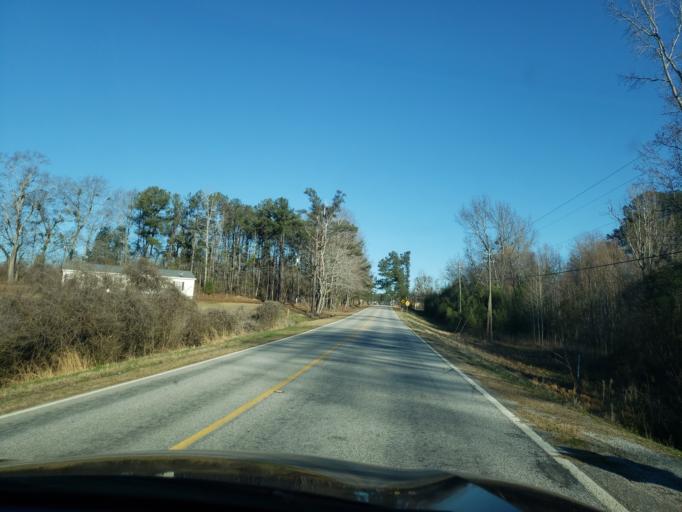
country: US
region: Alabama
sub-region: Elmore County
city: Tallassee
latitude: 32.5989
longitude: -85.8017
